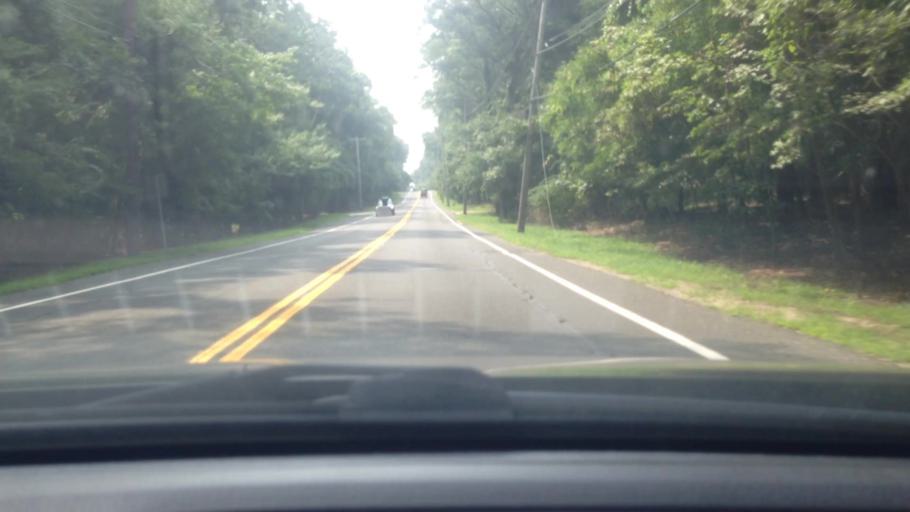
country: US
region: New York
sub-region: Suffolk County
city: Sag Harbor
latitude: 40.9754
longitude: -72.3020
